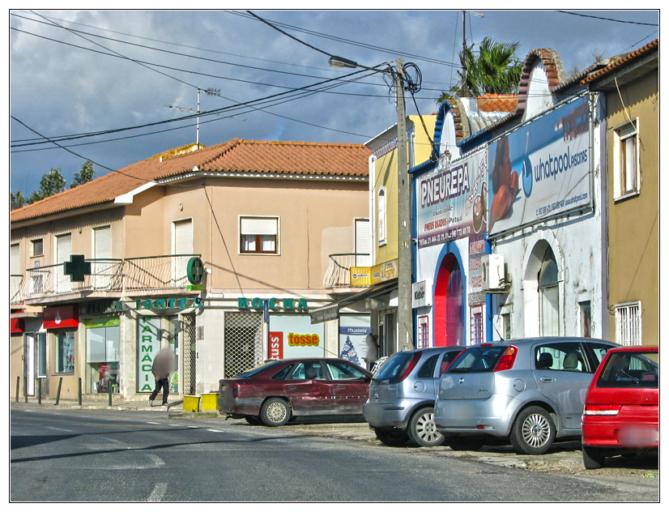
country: PT
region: Lisbon
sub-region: Cascais
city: Sao Domingos de Rana
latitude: 38.7365
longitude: -9.3392
